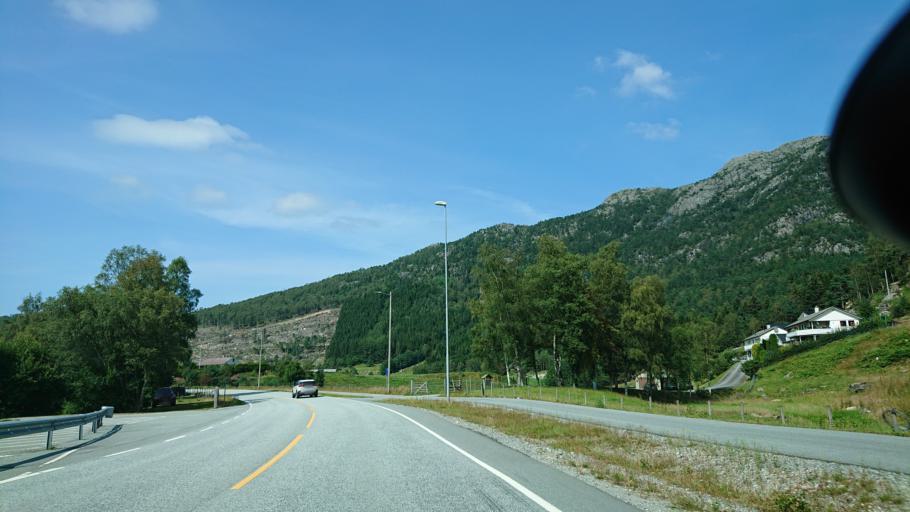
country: NO
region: Rogaland
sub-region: Strand
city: Jorpeland
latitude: 59.0731
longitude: 6.0477
